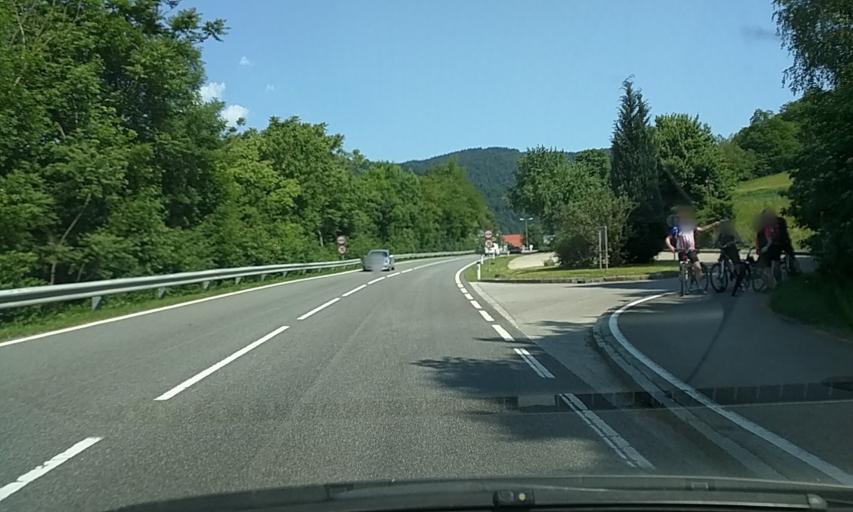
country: AT
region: Lower Austria
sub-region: Politischer Bezirk Krems
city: Aggsbach
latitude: 48.2613
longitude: 15.3781
